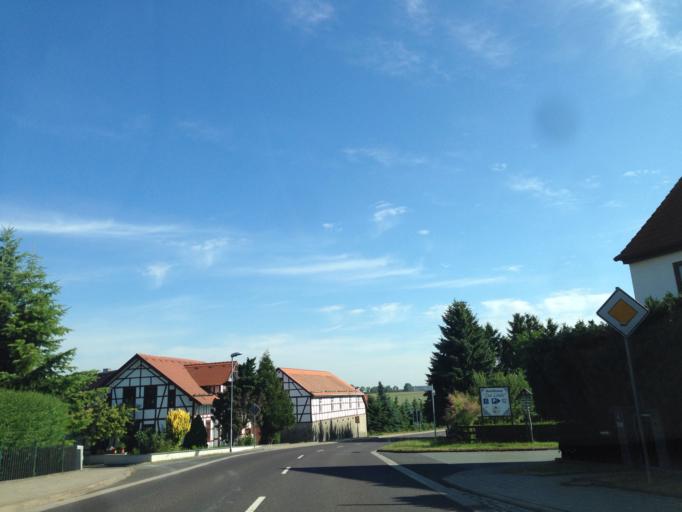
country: DE
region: Thuringia
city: Schwarza
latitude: 50.8126
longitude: 11.3361
